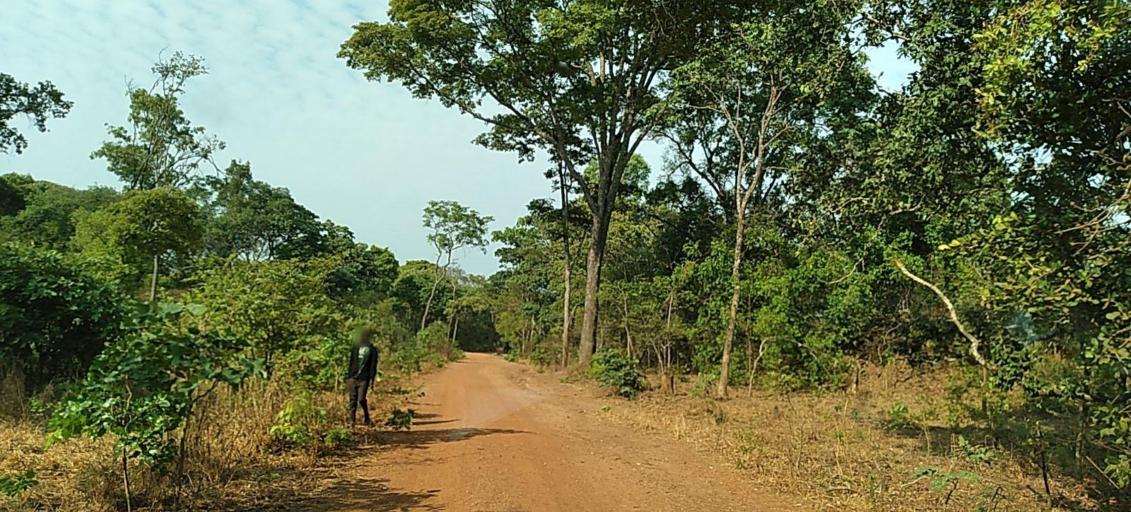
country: ZM
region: Copperbelt
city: Kalulushi
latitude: -12.9979
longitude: 27.7097
